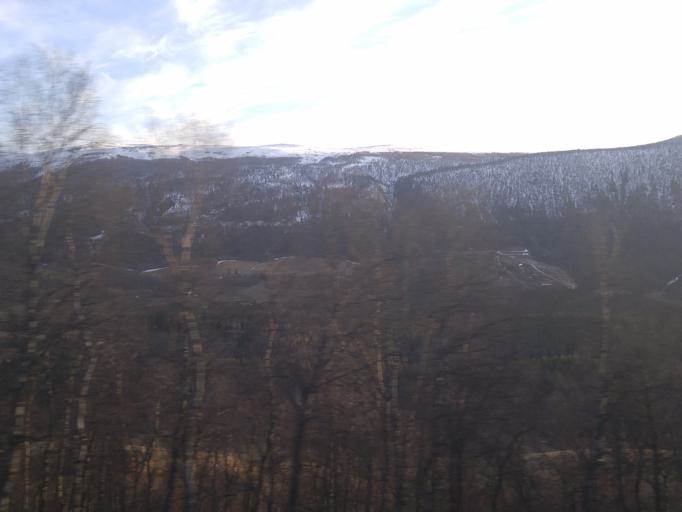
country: NO
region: Oppland
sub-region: Dovre
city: Dombas
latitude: 62.0576
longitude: 9.1321
